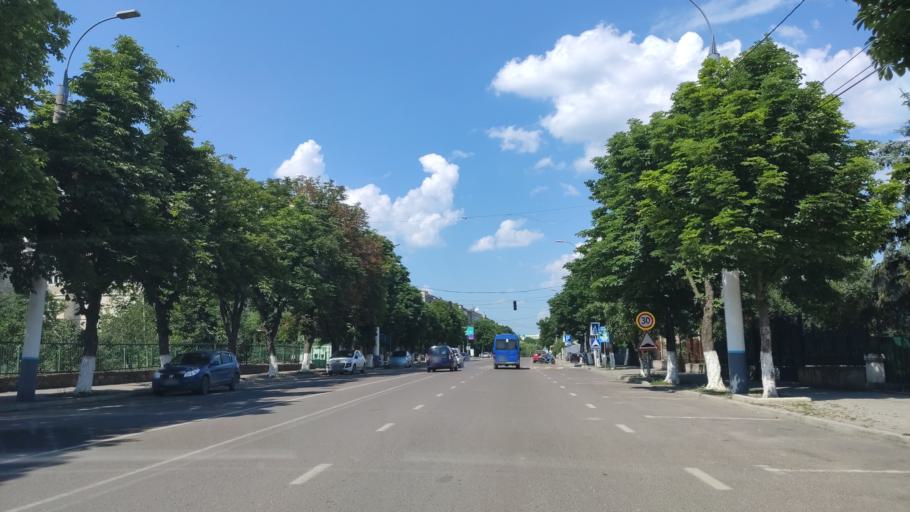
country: MD
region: Raionul Soroca
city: Soroca
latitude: 48.1589
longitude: 28.3026
